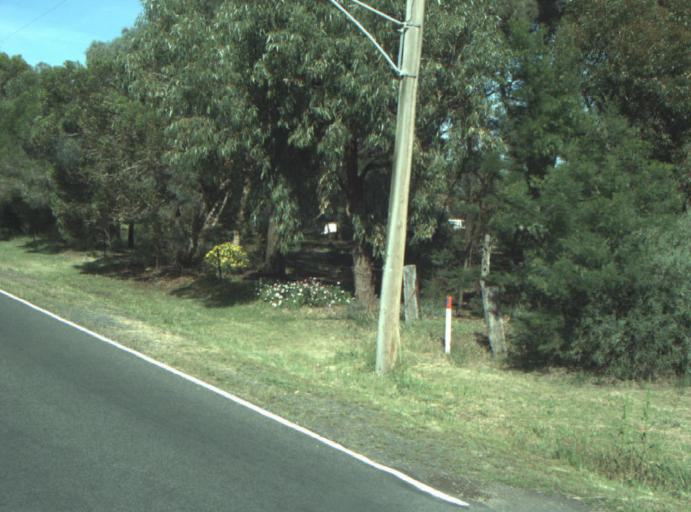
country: AU
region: Victoria
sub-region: Greater Geelong
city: Lara
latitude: -38.0058
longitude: 144.4346
